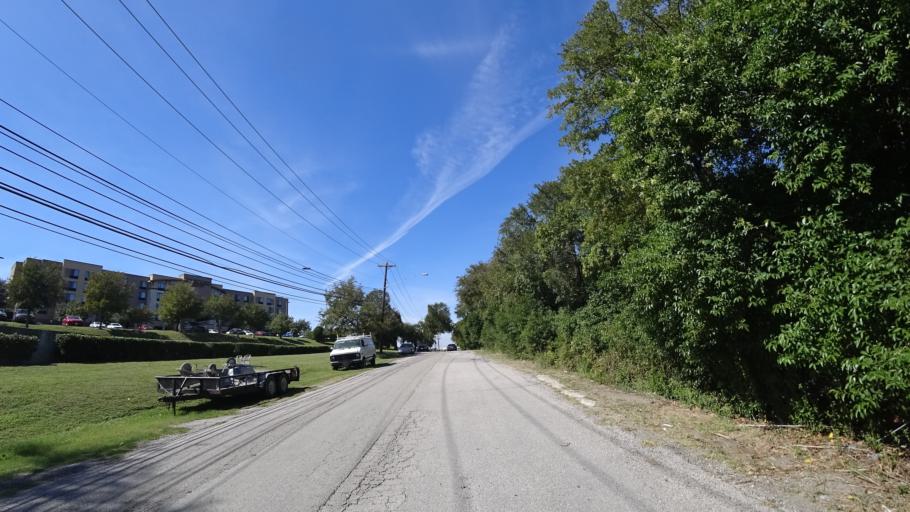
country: US
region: Texas
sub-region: Travis County
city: Austin
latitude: 30.2174
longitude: -97.6860
